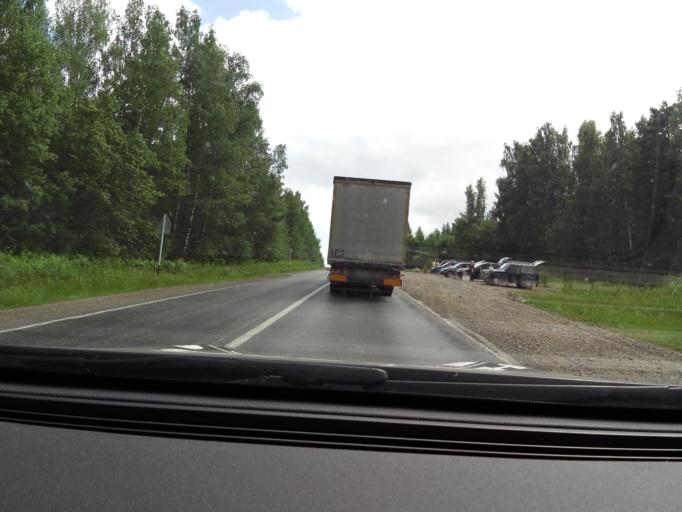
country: RU
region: Perm
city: Suksun
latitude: 57.0905
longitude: 57.3935
